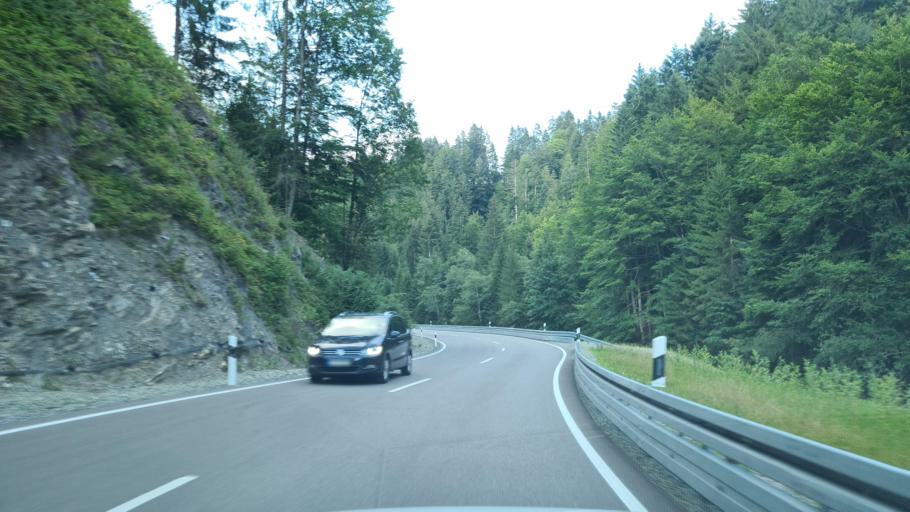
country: DE
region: Bavaria
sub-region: Swabia
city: Obermaiselstein
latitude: 47.4404
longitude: 10.2275
